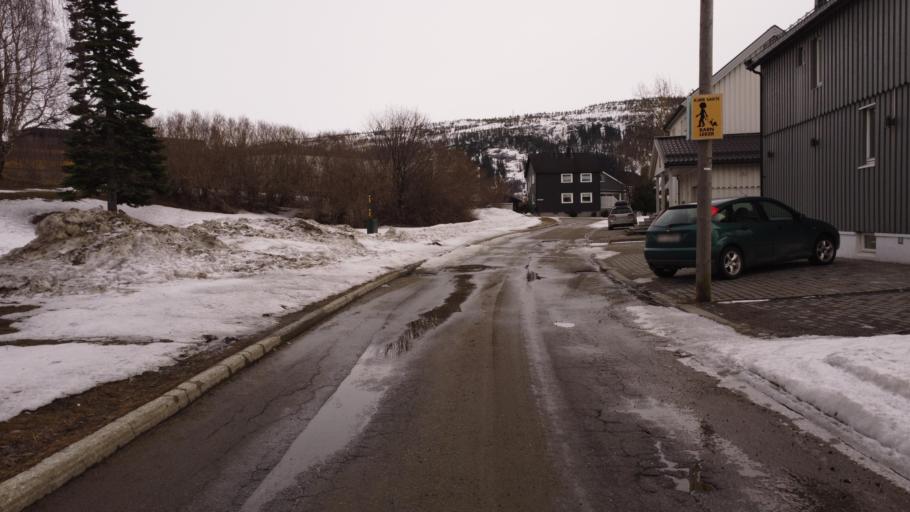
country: NO
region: Nordland
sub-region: Rana
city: Mo i Rana
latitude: 66.3143
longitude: 14.1546
